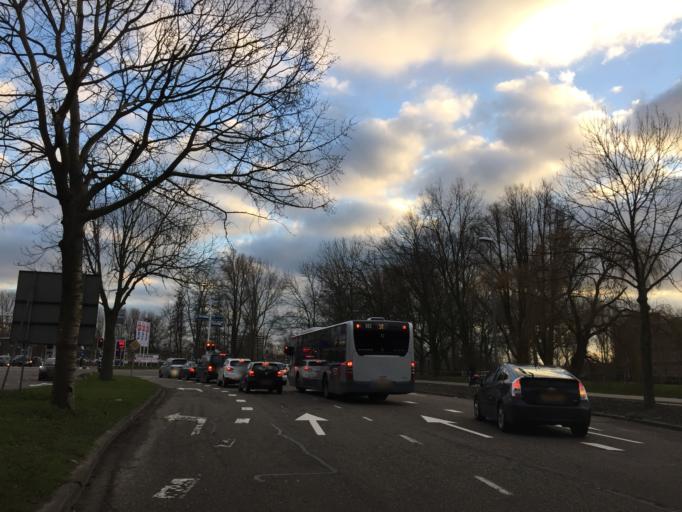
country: NL
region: South Holland
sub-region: Gemeente Schiedam
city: Schiedam
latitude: 51.9256
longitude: 4.3763
